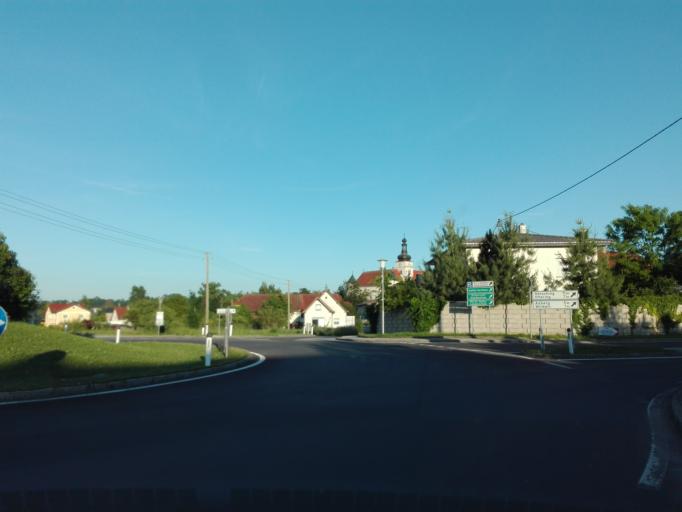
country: AT
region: Upper Austria
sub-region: Politischer Bezirk Urfahr-Umgebung
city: Goldworth
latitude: 48.2828
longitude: 14.1108
